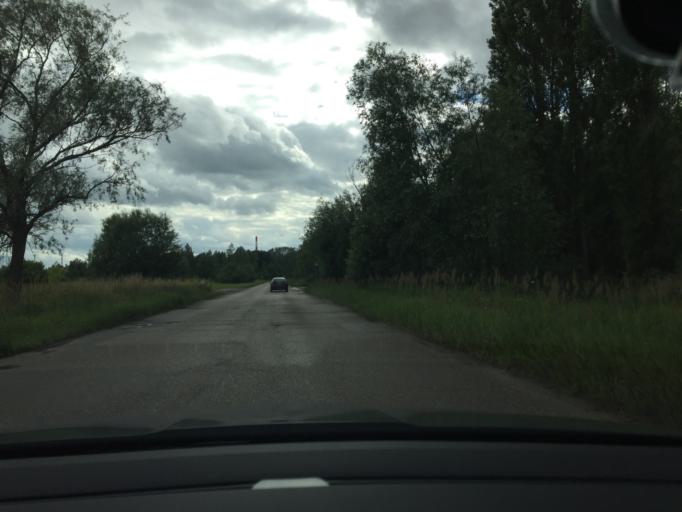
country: PL
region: Pomeranian Voivodeship
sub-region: Gdansk
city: Gdansk
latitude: 54.3539
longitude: 18.7583
